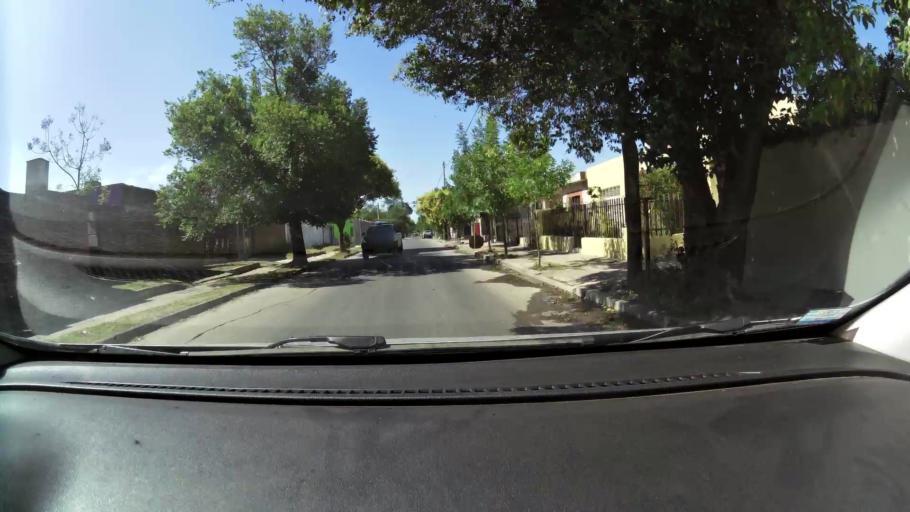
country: AR
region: Cordoba
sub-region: Departamento de Capital
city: Cordoba
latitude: -31.3747
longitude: -64.1566
